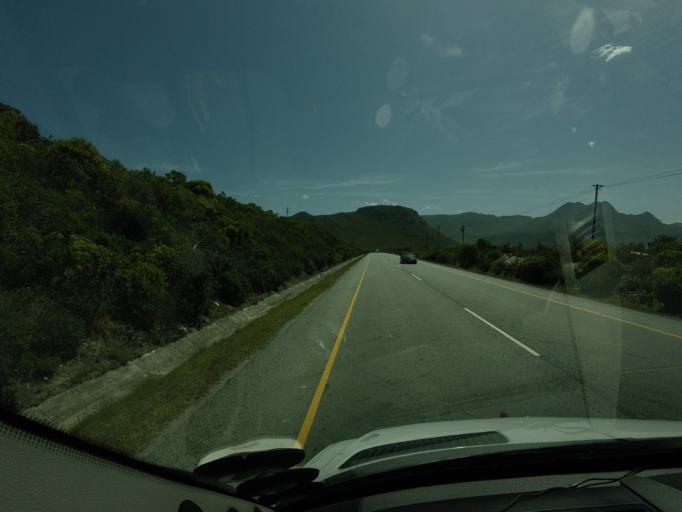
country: ZA
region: Western Cape
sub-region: Overberg District Municipality
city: Grabouw
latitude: -34.3531
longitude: 18.9741
